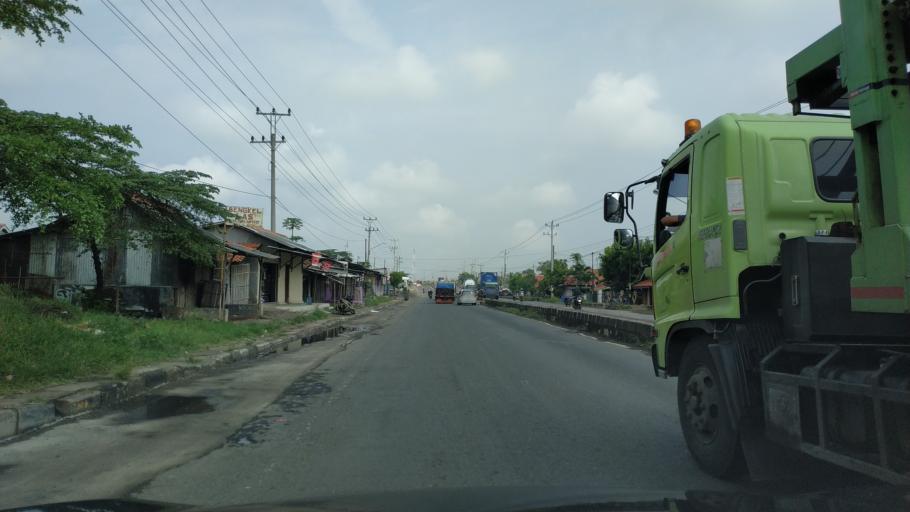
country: ID
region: Central Java
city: Bulakamba
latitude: -6.8713
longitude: 108.8948
